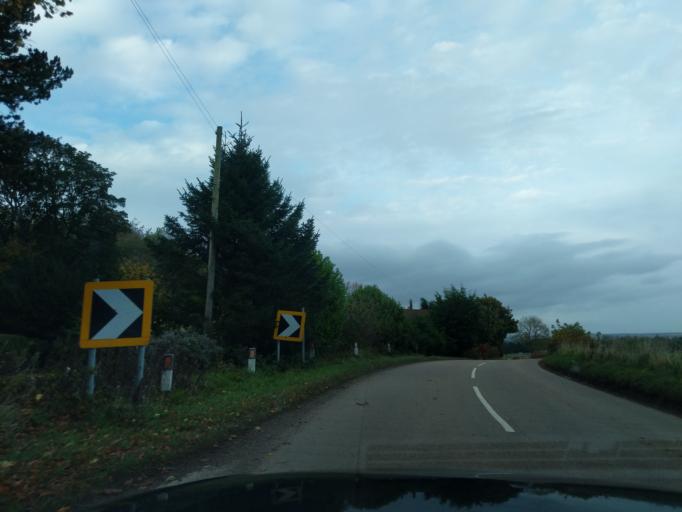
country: GB
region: Scotland
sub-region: Fife
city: Tayport
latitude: 56.4283
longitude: -2.8884
